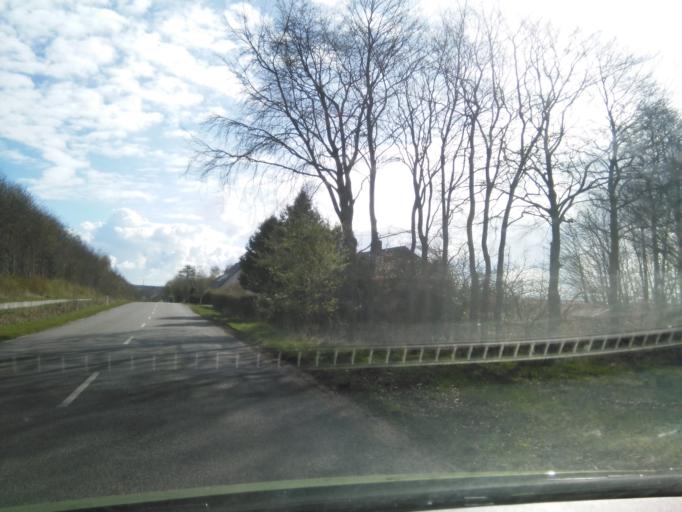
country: DK
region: Central Jutland
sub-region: Arhus Kommune
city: Trige
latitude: 56.2237
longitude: 10.1736
